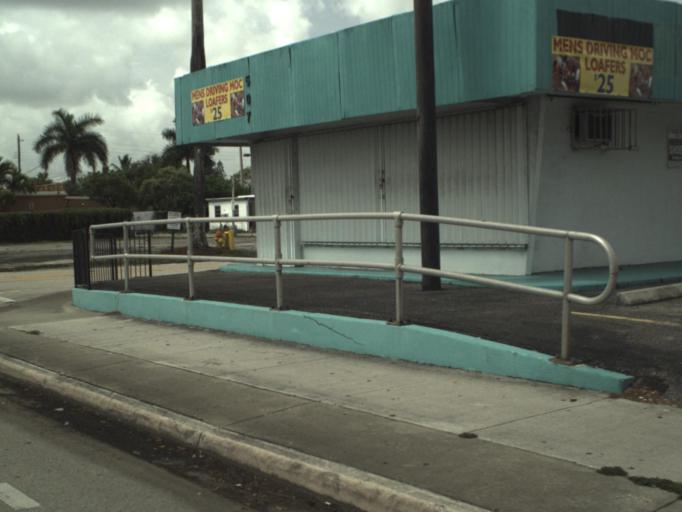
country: US
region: Florida
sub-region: Broward County
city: Hallandale Beach
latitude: 25.9918
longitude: -80.1426
